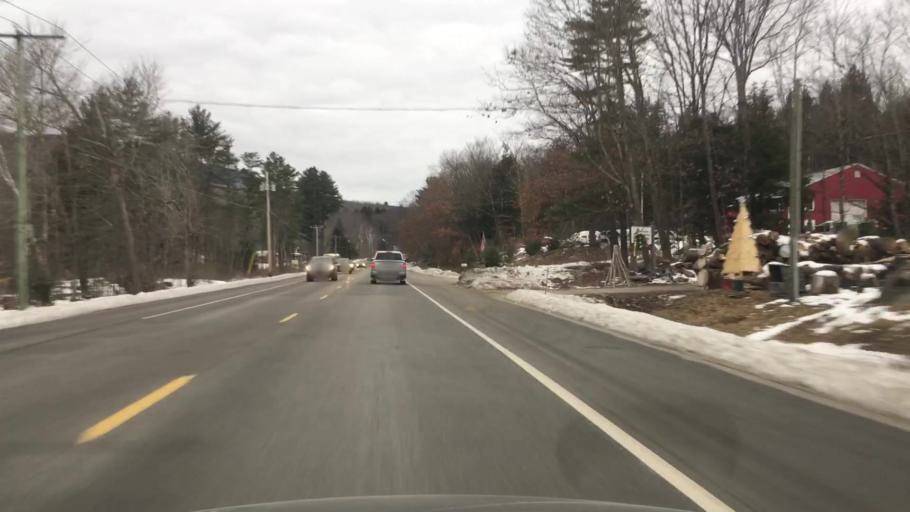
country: US
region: New Hampshire
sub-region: Merrimack County
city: Newbury
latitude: 43.3023
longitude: -72.0067
